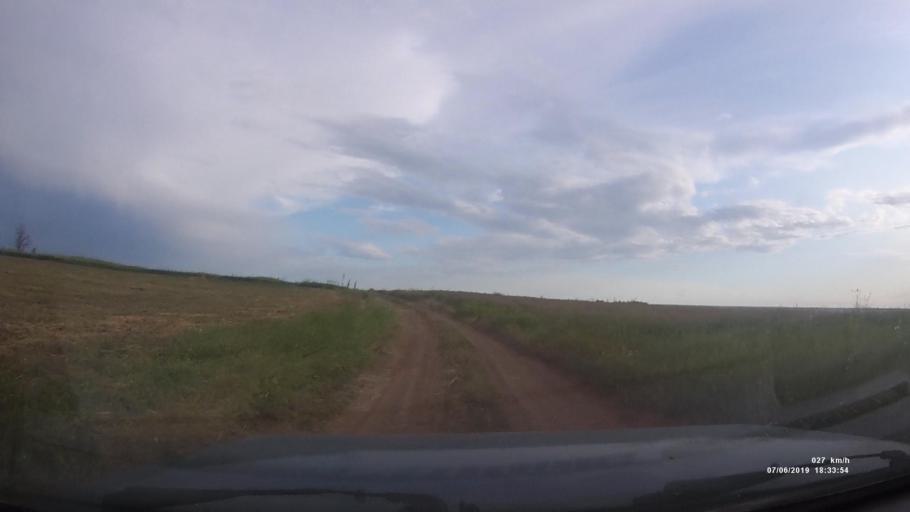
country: RU
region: Rostov
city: Staraya Stanitsa
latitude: 48.2598
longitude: 40.3621
